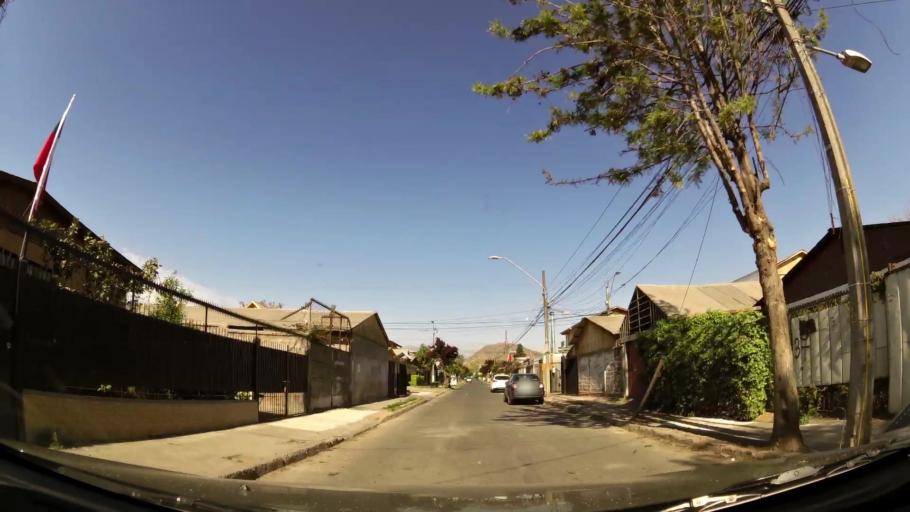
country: CL
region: Santiago Metropolitan
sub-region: Provincia de Maipo
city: San Bernardo
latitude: -33.6132
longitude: -70.7006
